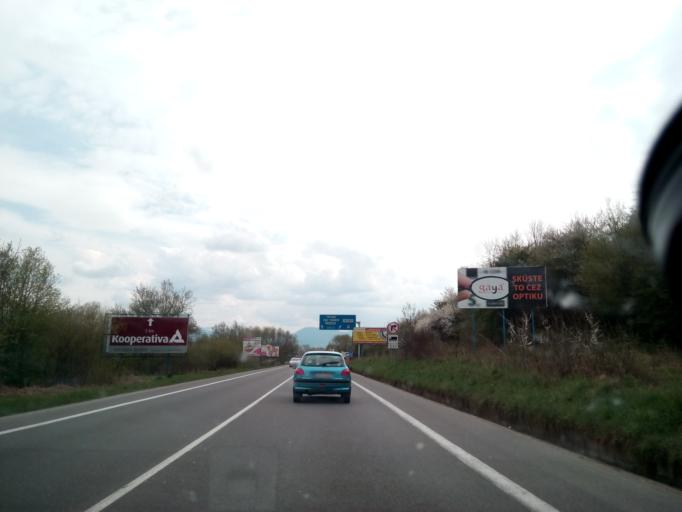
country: SK
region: Zilinsky
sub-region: Okres Zilina
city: Vrutky
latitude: 49.1032
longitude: 18.9184
